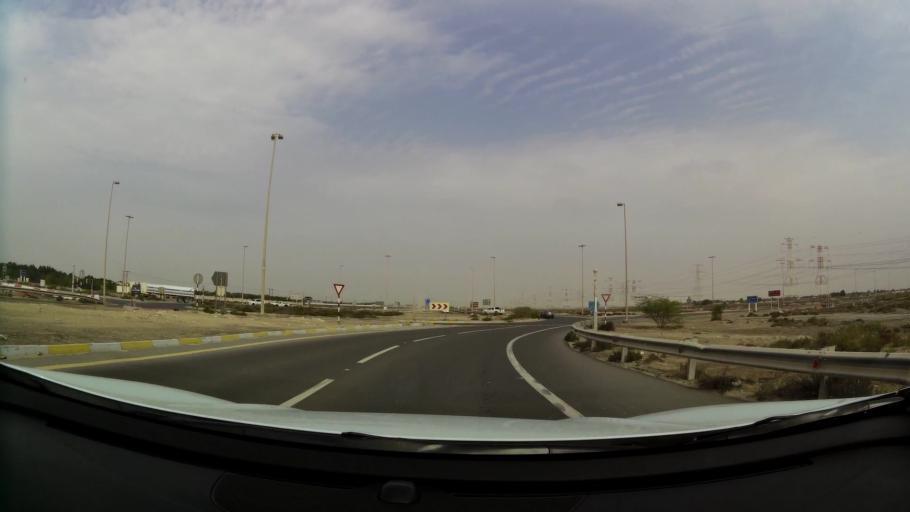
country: AE
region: Abu Dhabi
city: Abu Dhabi
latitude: 24.6647
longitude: 54.7417
